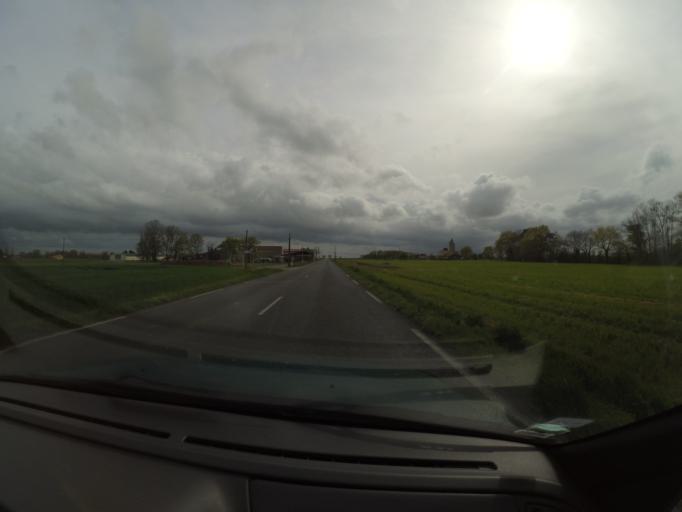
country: FR
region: Pays de la Loire
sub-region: Departement de Maine-et-Loire
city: Saint-Laurent-des-Autels
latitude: 47.2608
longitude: -1.2027
